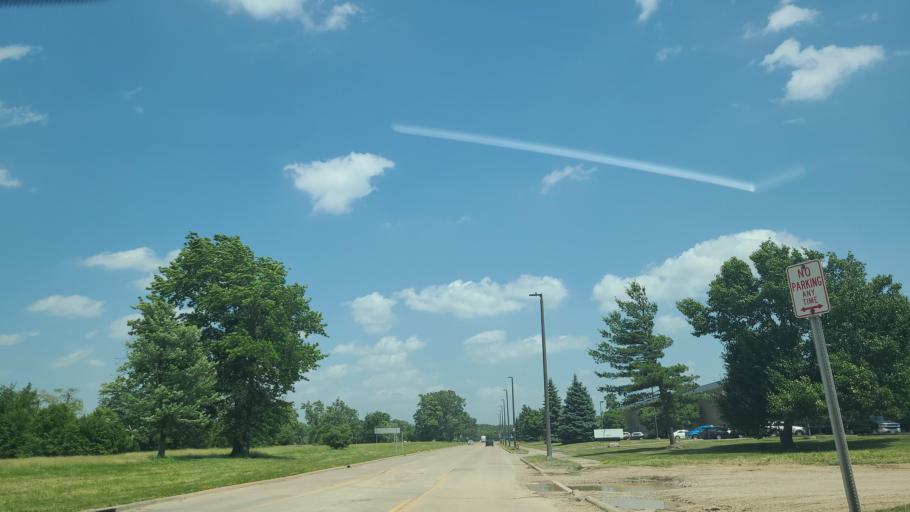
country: US
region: Ohio
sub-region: Cuyahoga County
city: Fairview Park
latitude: 41.4252
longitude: -81.8331
